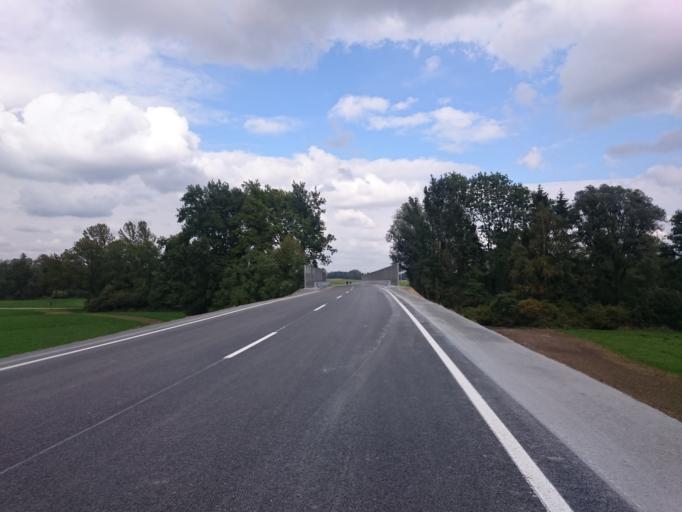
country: DE
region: Bavaria
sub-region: Upper Bavaria
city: Kolbermoor
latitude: 47.8256
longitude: 12.0751
